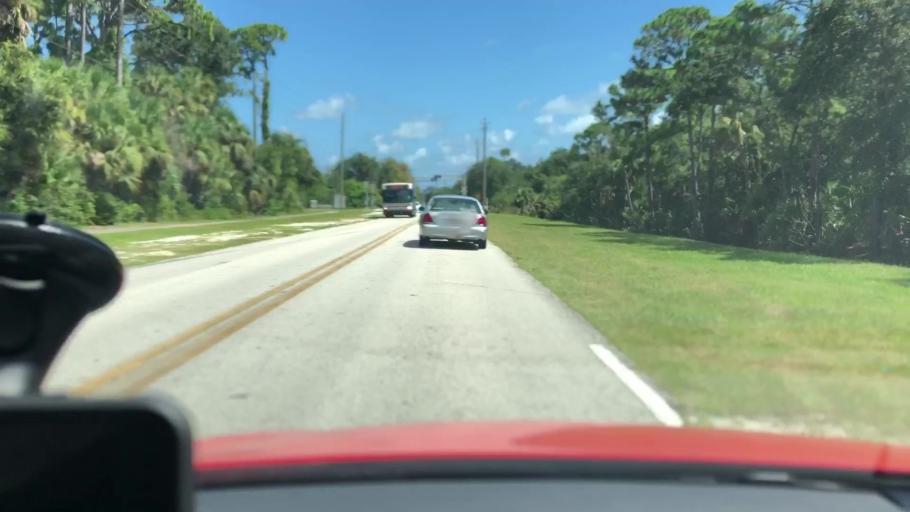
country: US
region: Florida
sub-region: Volusia County
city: Edgewater
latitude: 29.0033
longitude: -80.9197
